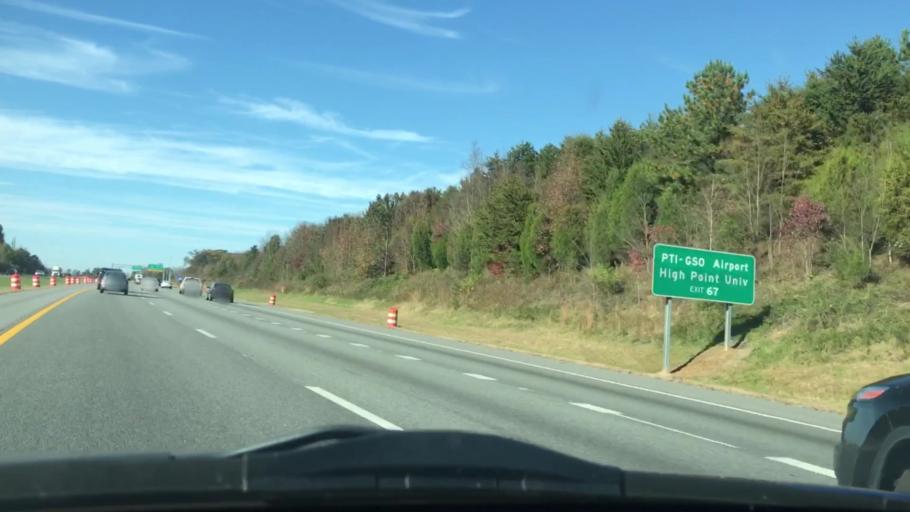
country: US
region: North Carolina
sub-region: Guilford County
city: High Point
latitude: 35.9946
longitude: -79.9862
